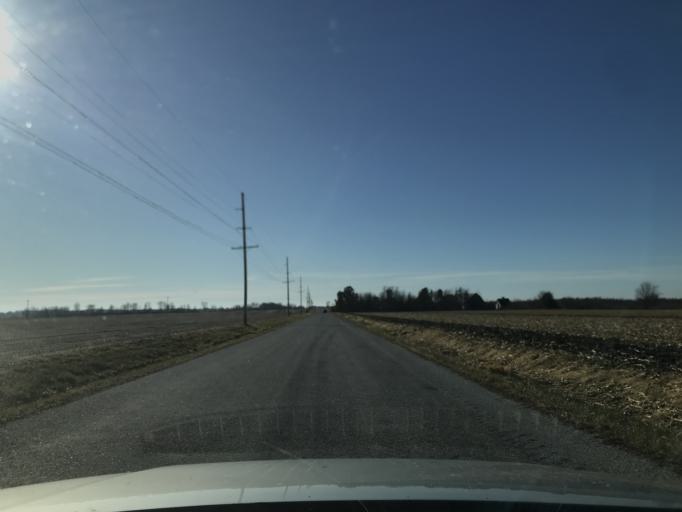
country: US
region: Illinois
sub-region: Hancock County
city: Carthage
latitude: 40.4716
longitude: -91.1782
